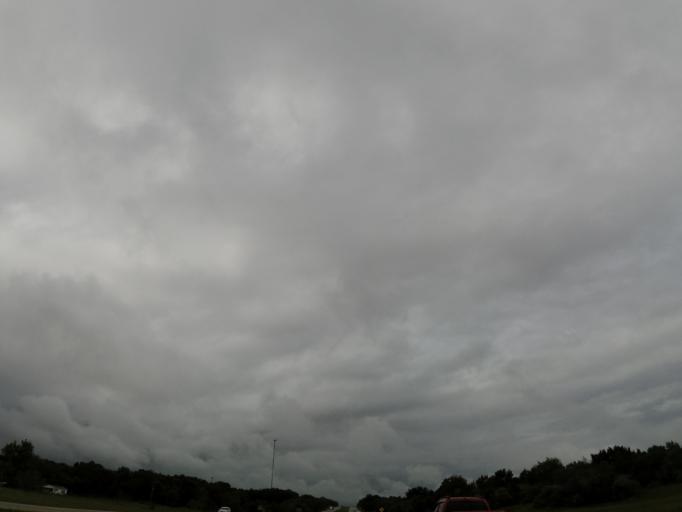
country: US
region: Illinois
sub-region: Jefferson County
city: Mount Vernon
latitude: 38.3622
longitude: -89.0361
